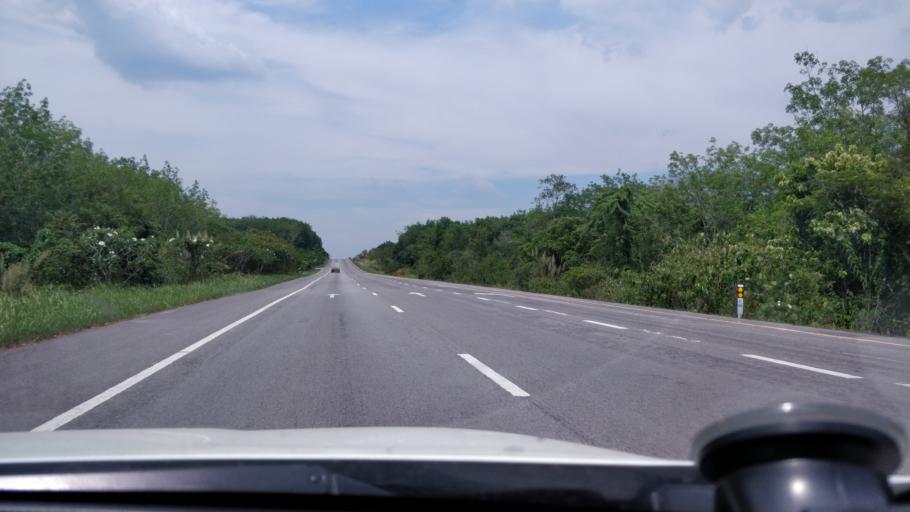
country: TH
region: Surat Thani
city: Khian Sa
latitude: 8.7034
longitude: 99.1434
